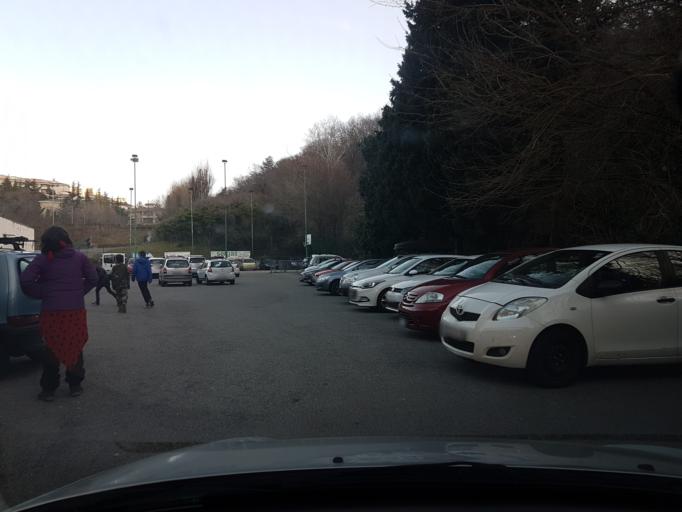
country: IT
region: Friuli Venezia Giulia
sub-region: Provincia di Trieste
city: Trieste
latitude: 45.6538
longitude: 13.8011
